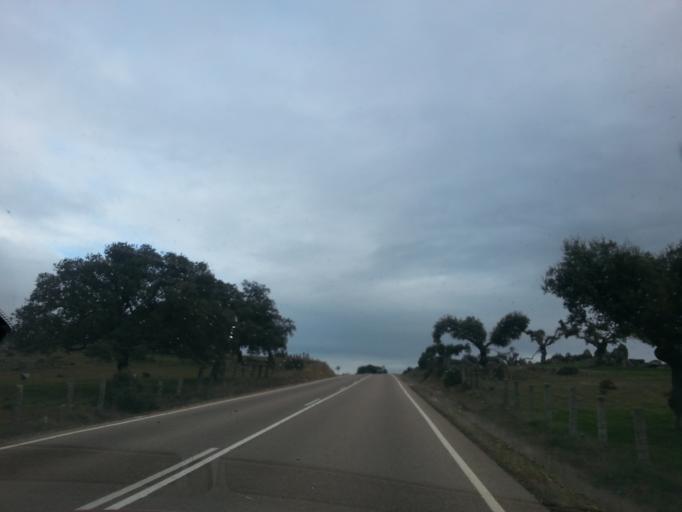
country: ES
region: Castille and Leon
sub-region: Provincia de Salamanca
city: Berrocal de Huebra
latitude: 40.7052
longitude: -6.0107
